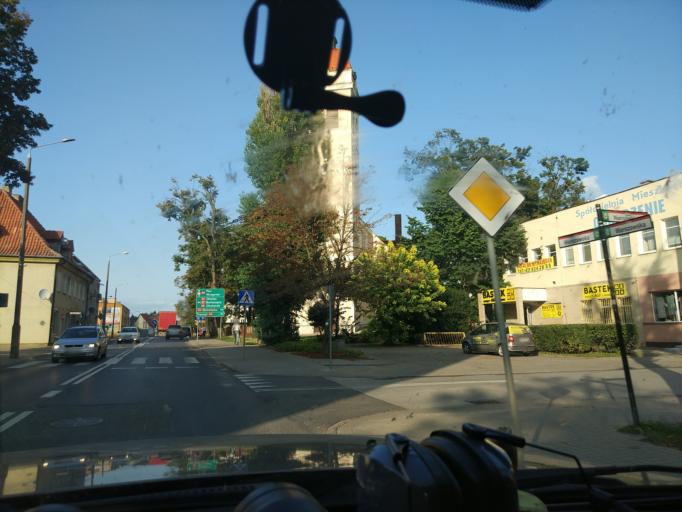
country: PL
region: Warmian-Masurian Voivodeship
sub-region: Powiat szczycienski
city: Szczytno
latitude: 53.5625
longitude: 20.9938
